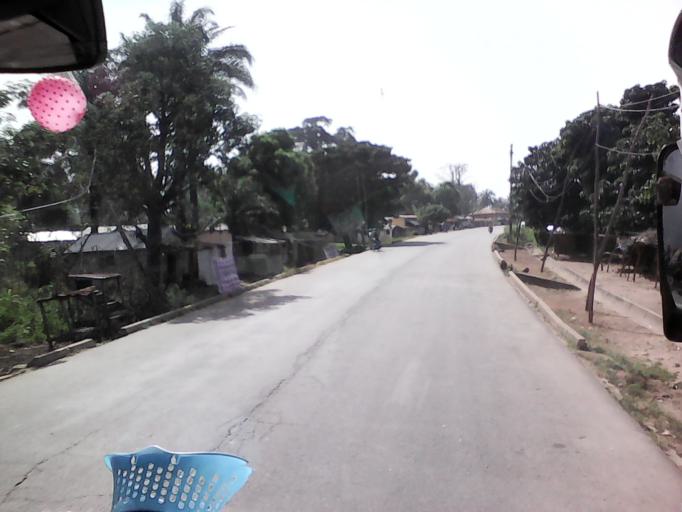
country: TG
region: Centrale
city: Sokode
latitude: 8.8342
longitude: 1.0785
